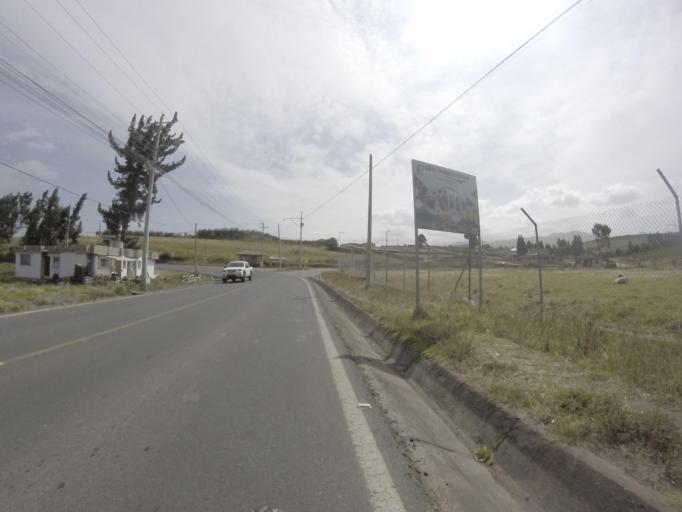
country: EC
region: Pichincha
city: Cayambe
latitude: 0.1320
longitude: -78.0819
